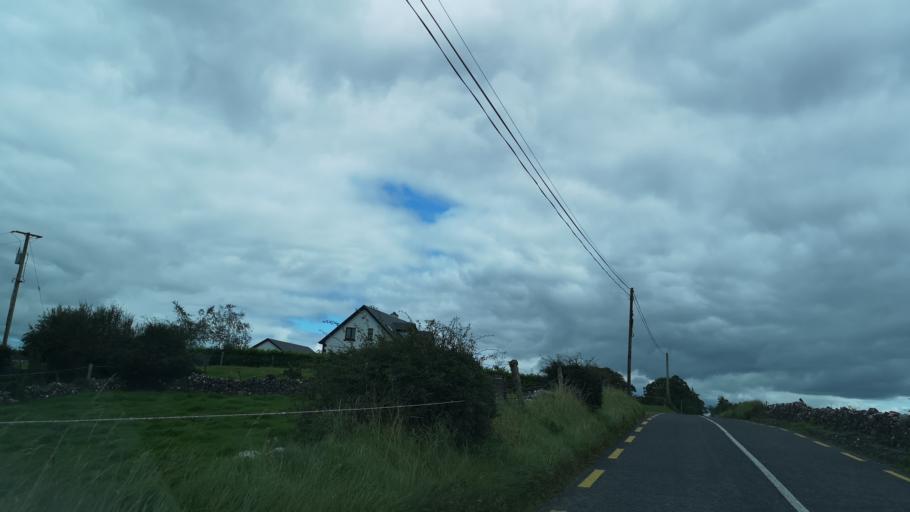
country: IE
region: Connaught
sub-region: County Galway
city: Ballinasloe
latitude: 53.2962
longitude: -8.1118
